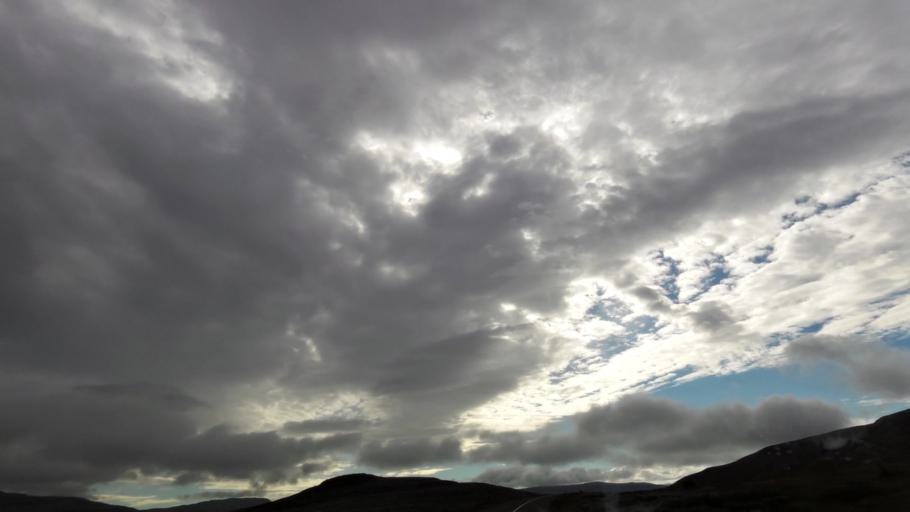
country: IS
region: West
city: Olafsvik
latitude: 65.5381
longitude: -23.8207
